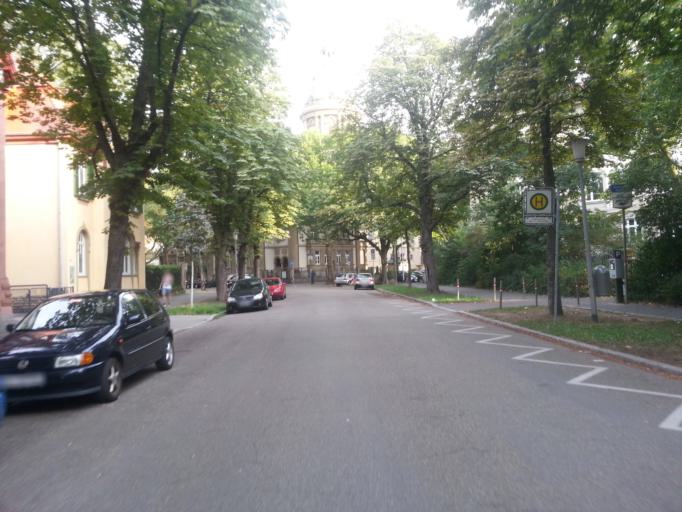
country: DE
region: Baden-Wuerttemberg
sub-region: Karlsruhe Region
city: Mannheim
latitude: 49.4857
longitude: 8.4803
